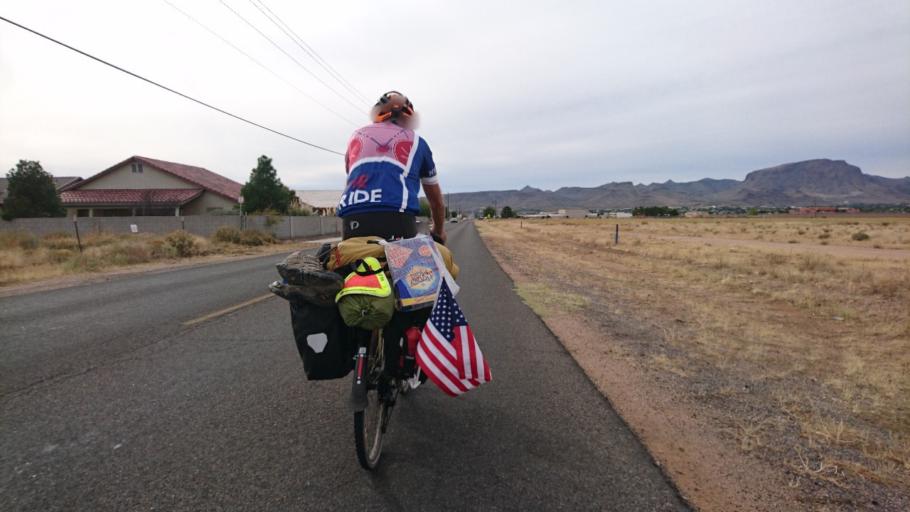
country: US
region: Arizona
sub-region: Mohave County
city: New Kingman-Butler
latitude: 35.2394
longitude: -113.9989
